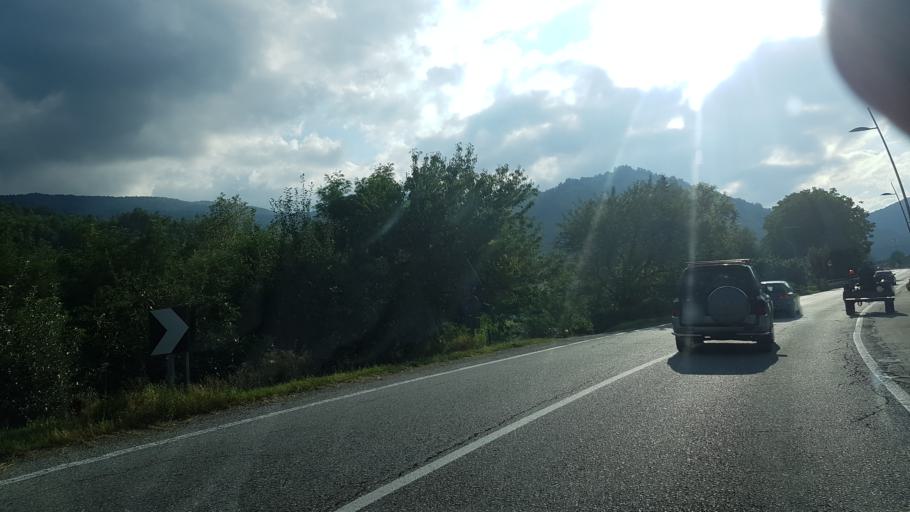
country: IT
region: Piedmont
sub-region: Provincia di Cuneo
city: Venasca
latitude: 44.5637
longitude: 7.4021
